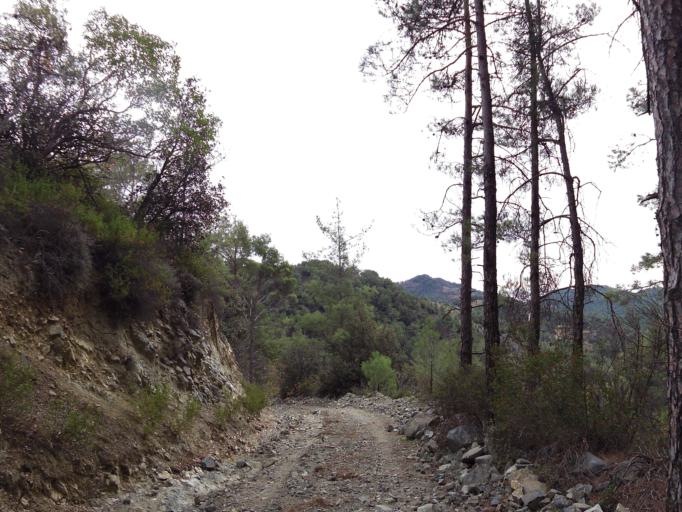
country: CY
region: Limassol
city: Kyperounta
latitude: 34.9297
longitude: 32.9431
